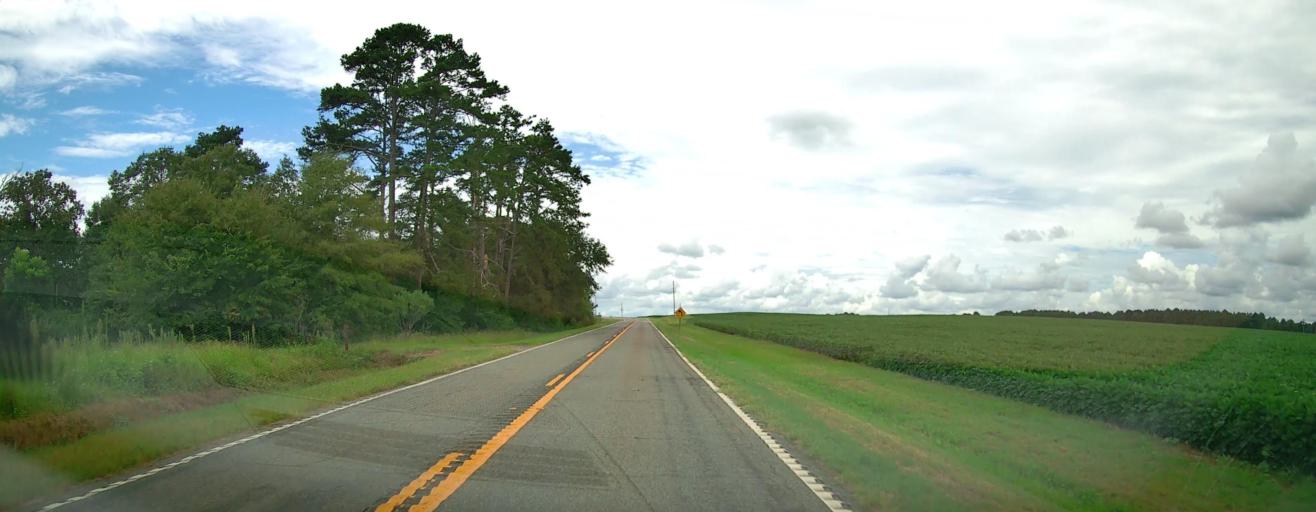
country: US
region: Georgia
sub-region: Dooly County
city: Unadilla
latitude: 32.2867
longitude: -83.8263
